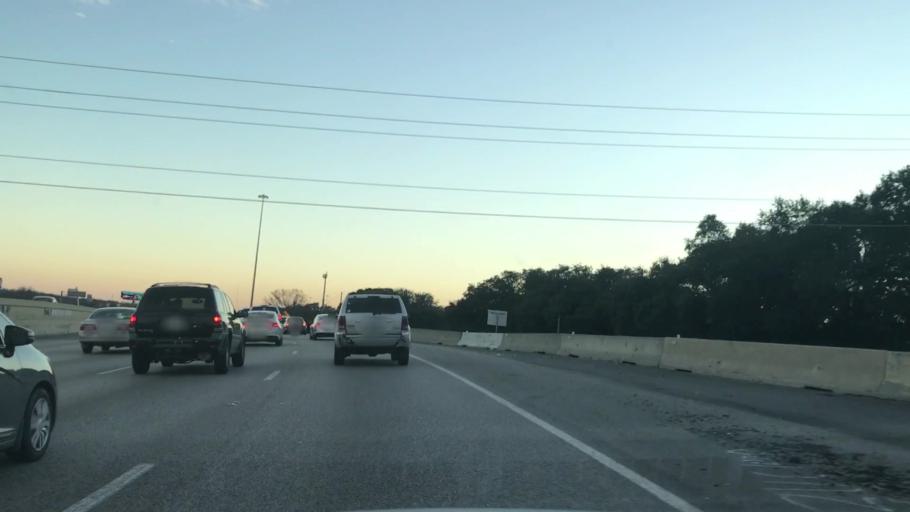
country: US
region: Texas
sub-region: Dallas County
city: Dallas
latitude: 32.7384
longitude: -96.8239
